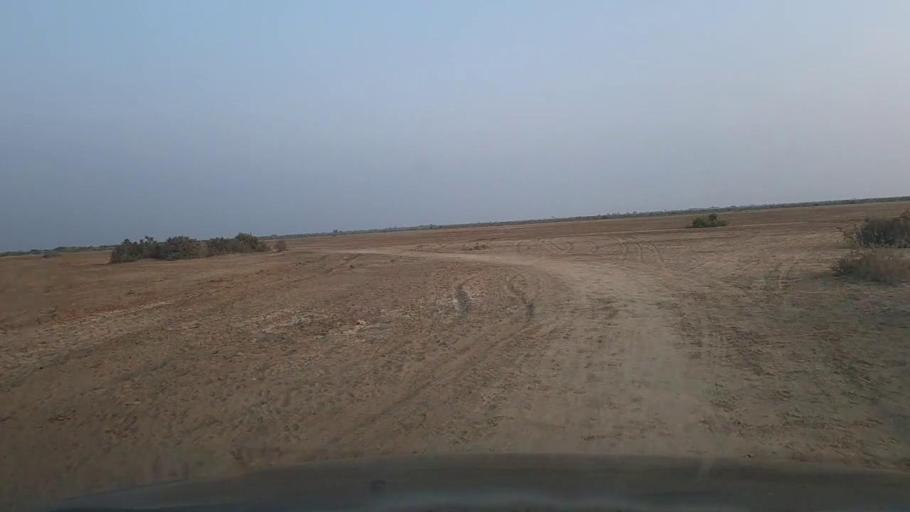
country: PK
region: Sindh
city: Jati
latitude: 24.5296
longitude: 68.4114
